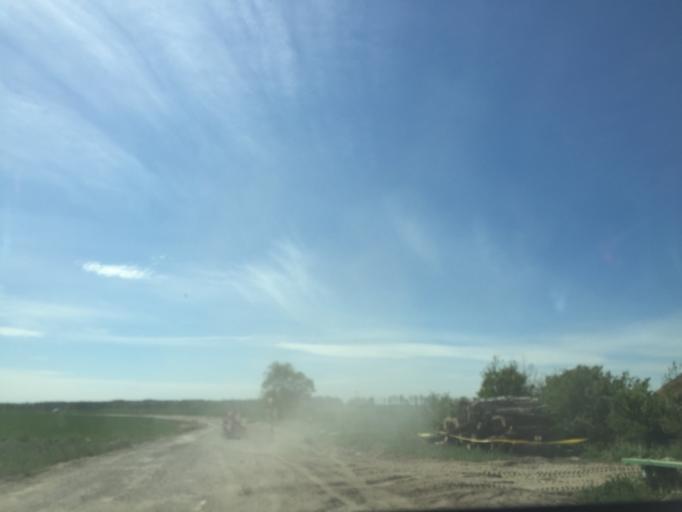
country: LT
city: Linkuva
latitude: 56.0608
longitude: 24.0822
